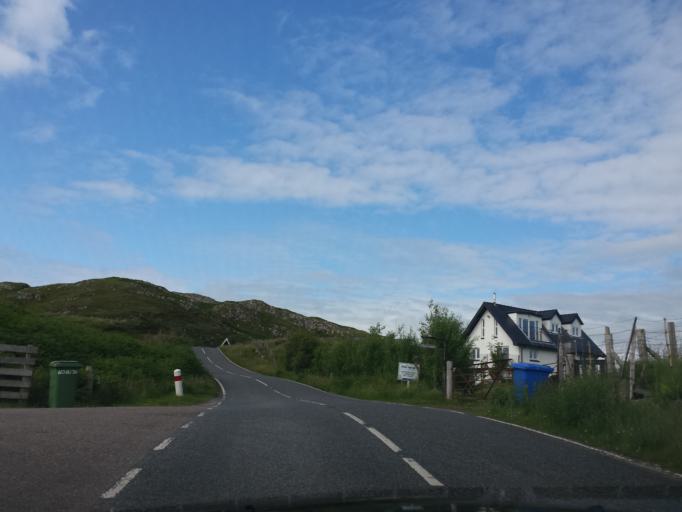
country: GB
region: Scotland
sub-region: Argyll and Bute
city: Isle Of Mull
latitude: 56.9578
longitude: -5.8419
